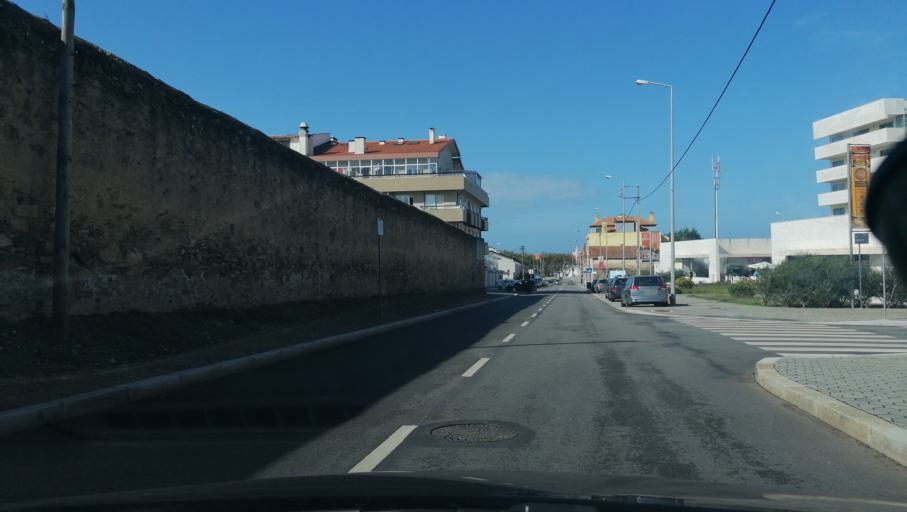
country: PT
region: Porto
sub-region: Vila Nova de Gaia
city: Arcozelo
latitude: 41.0404
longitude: -8.6446
